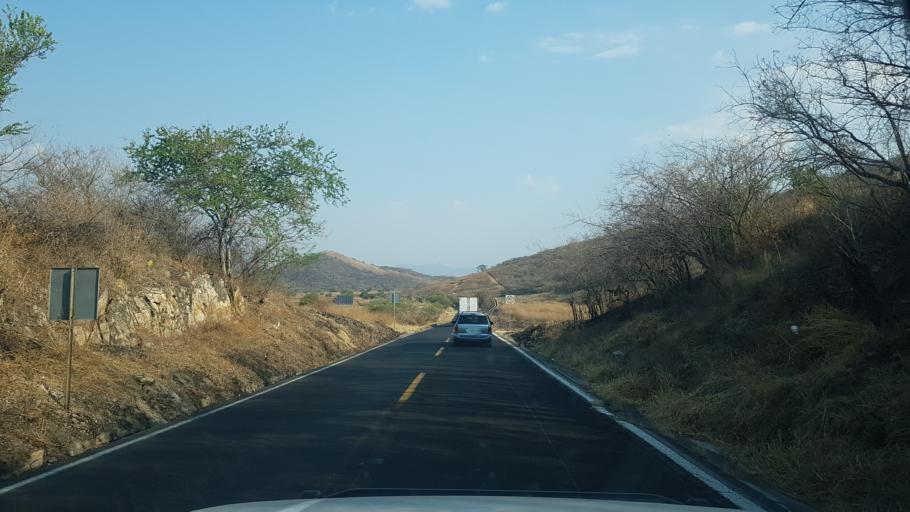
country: MX
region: Puebla
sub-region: Tilapa
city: San Felix Rijo
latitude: 18.6375
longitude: -98.5865
